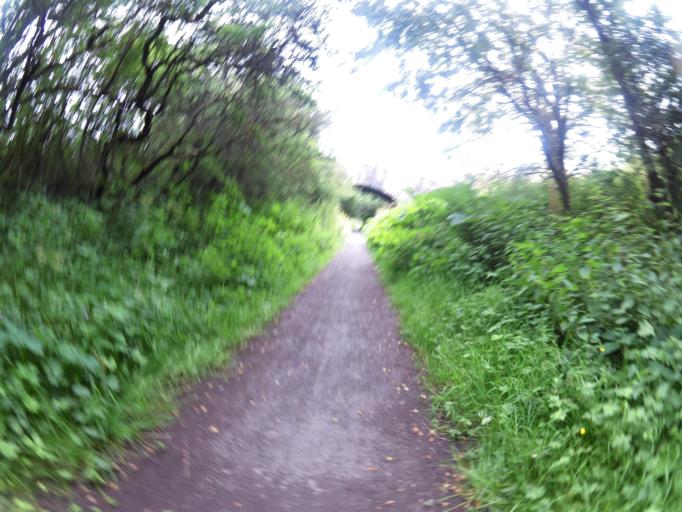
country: GB
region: Scotland
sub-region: Edinburgh
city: Kirkliston
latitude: 55.9478
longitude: -3.4009
